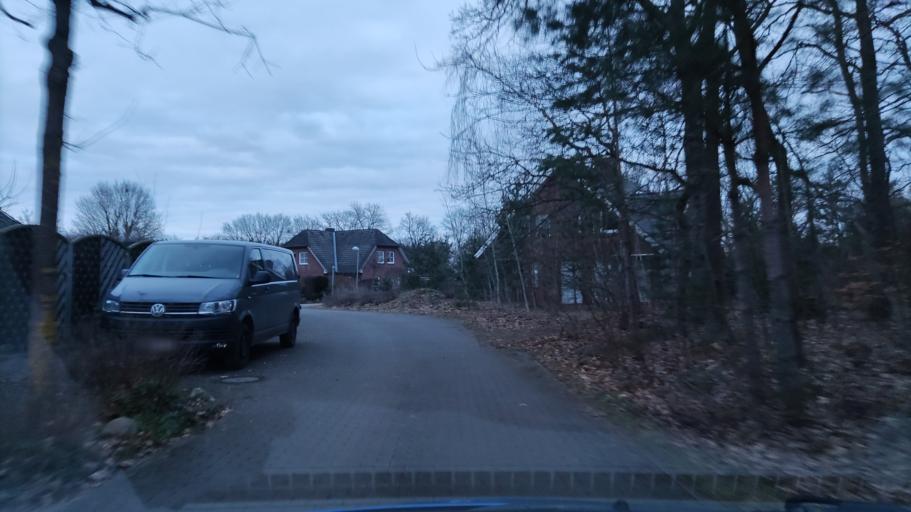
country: DE
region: Lower Saxony
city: Wendisch Evern
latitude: 53.2155
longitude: 10.4803
